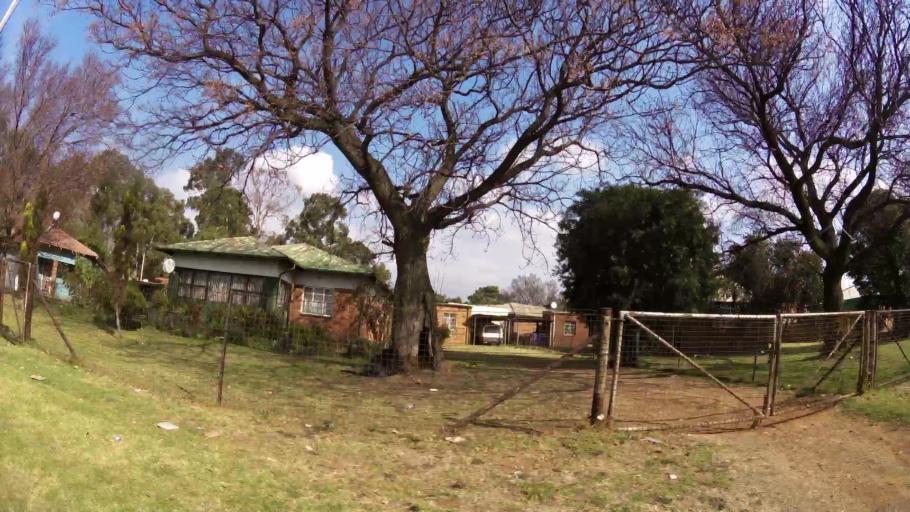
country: ZA
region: Gauteng
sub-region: Ekurhuleni Metropolitan Municipality
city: Boksburg
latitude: -26.1634
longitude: 28.2033
